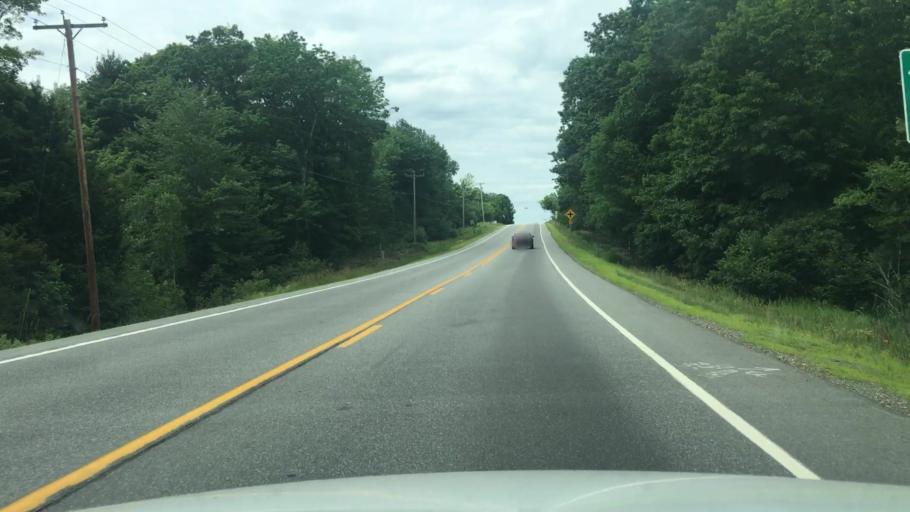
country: US
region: Maine
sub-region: Waldo County
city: Palermo
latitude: 44.4091
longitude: -69.5166
